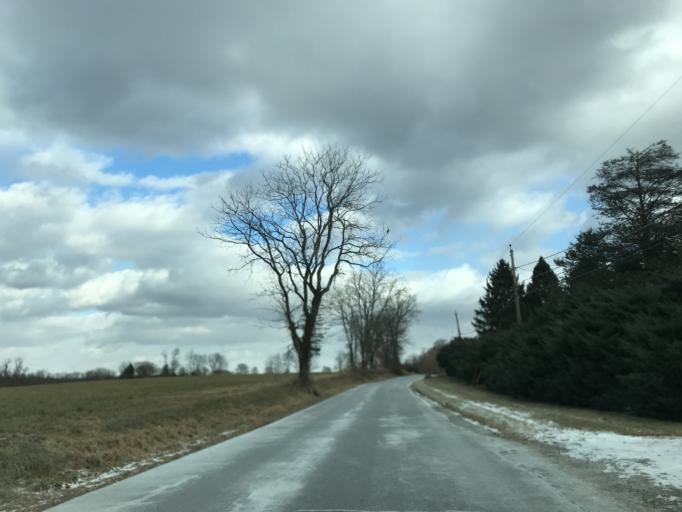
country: US
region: Maryland
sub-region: Harford County
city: Jarrettsville
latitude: 39.5741
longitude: -76.5717
